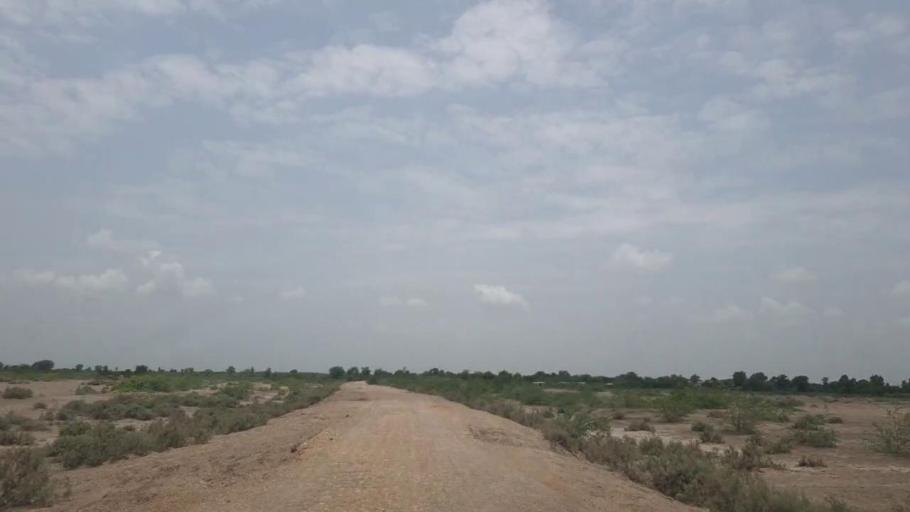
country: PK
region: Sindh
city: Naukot
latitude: 24.9409
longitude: 69.2034
